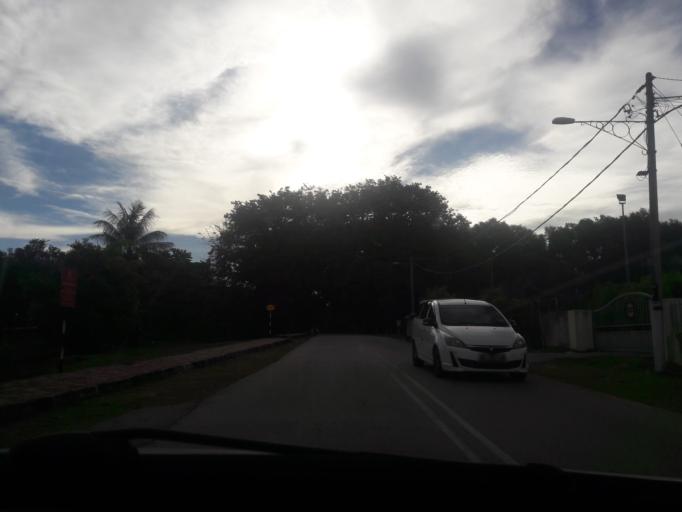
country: MY
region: Kedah
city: Sungai Petani
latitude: 5.6483
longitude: 100.4885
